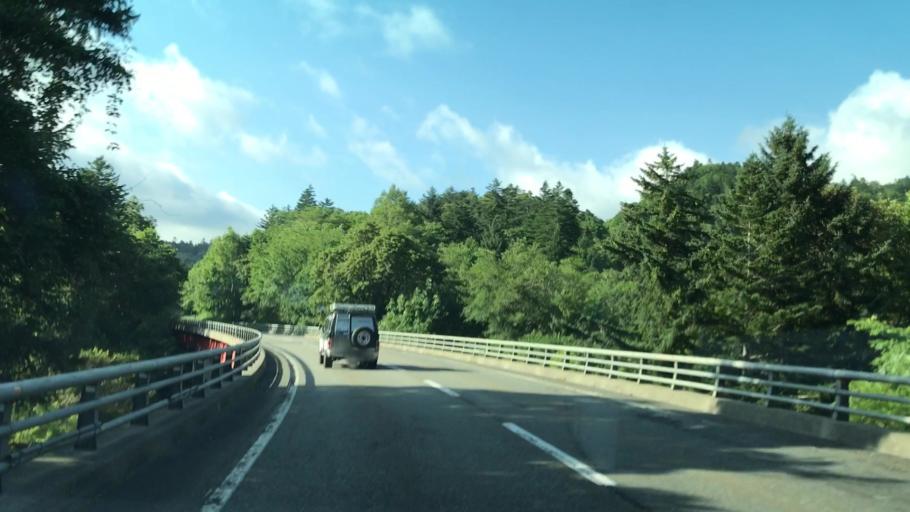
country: JP
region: Hokkaido
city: Iwamizawa
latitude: 42.9032
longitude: 142.1277
